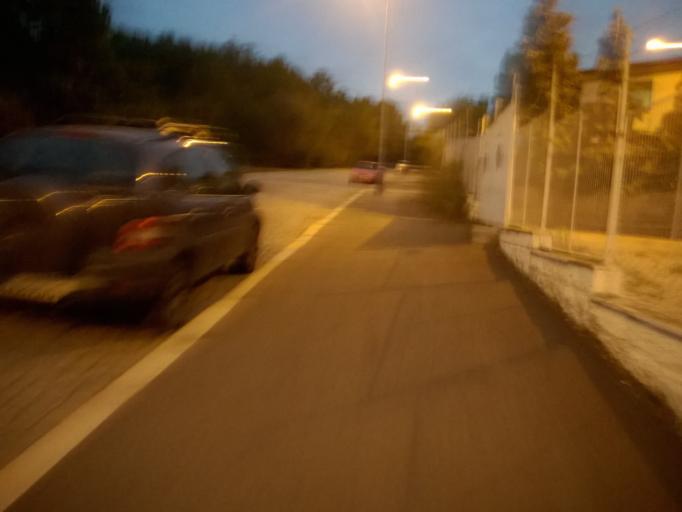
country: CZ
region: Praha
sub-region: Praha 9
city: Vysocany
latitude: 50.0990
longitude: 14.5055
